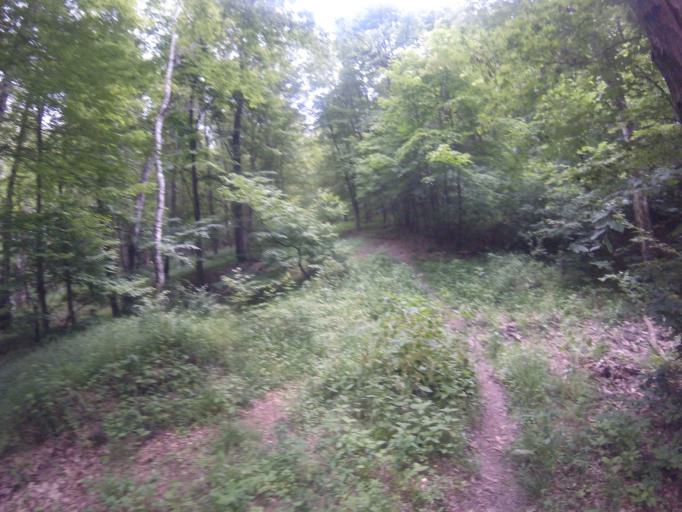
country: HU
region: Veszprem
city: Urkut
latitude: 47.0604
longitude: 17.6688
